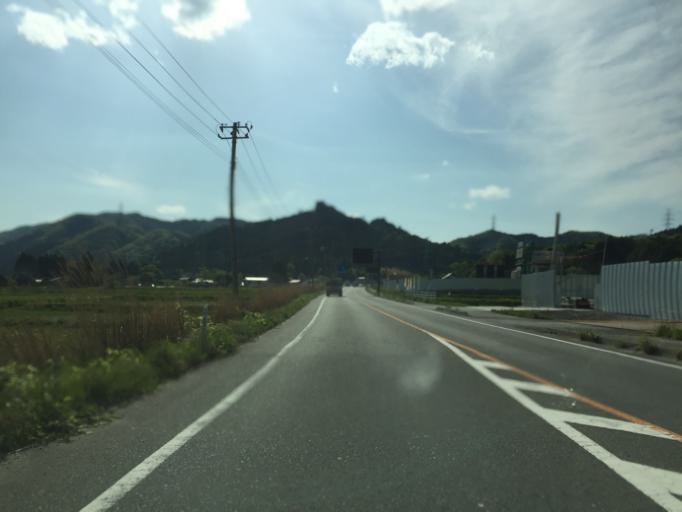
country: JP
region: Fukushima
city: Namie
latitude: 37.3707
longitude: 140.9644
